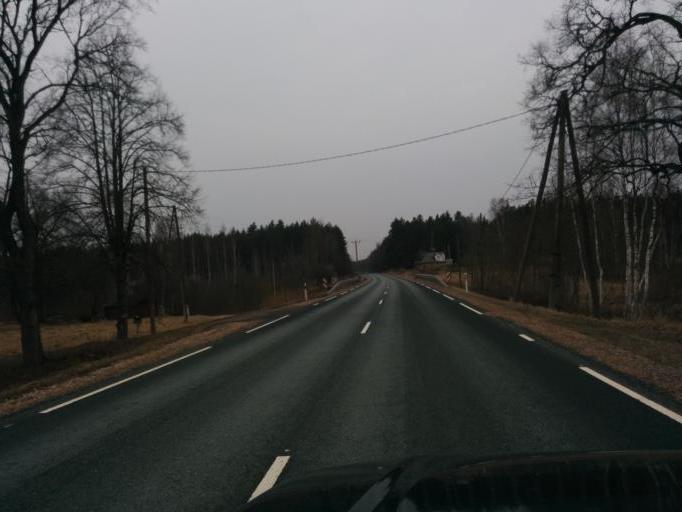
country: LV
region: Ogre
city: Ogre
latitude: 56.7902
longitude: 24.6057
